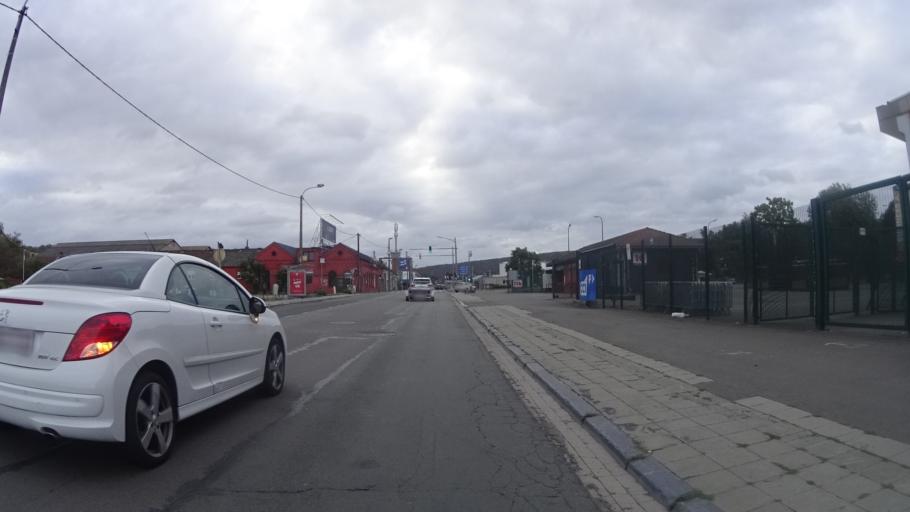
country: BE
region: Wallonia
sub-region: Province de Liege
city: Saint-Nicolas
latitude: 50.6109
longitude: 5.5441
